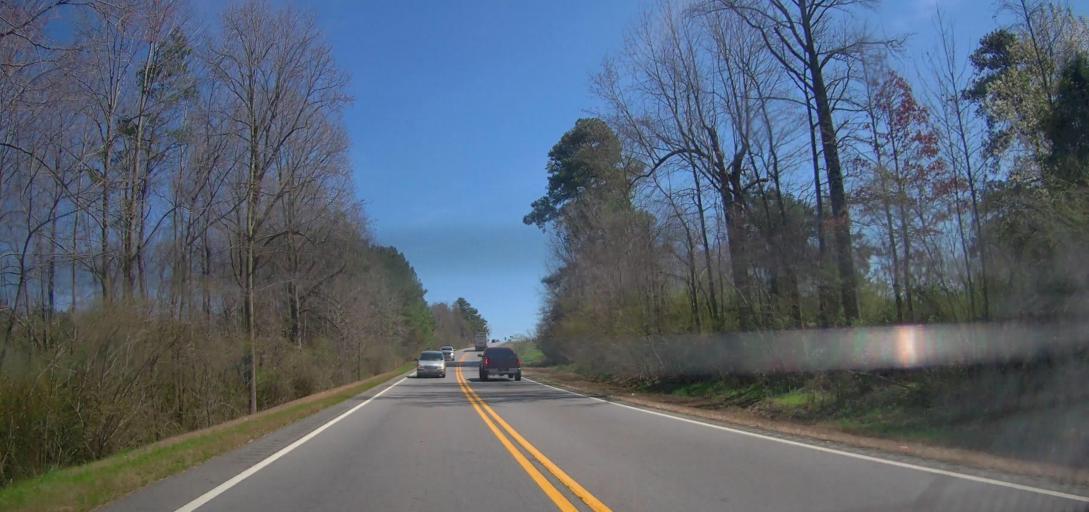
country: US
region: Alabama
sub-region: Blount County
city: Blountsville
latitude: 34.1729
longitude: -86.5301
